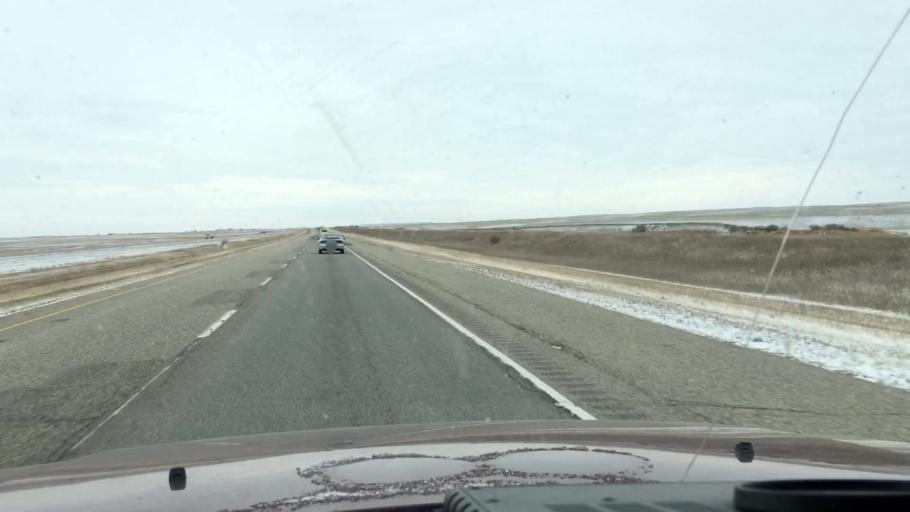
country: CA
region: Saskatchewan
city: Saskatoon
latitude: 51.4629
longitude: -106.2371
